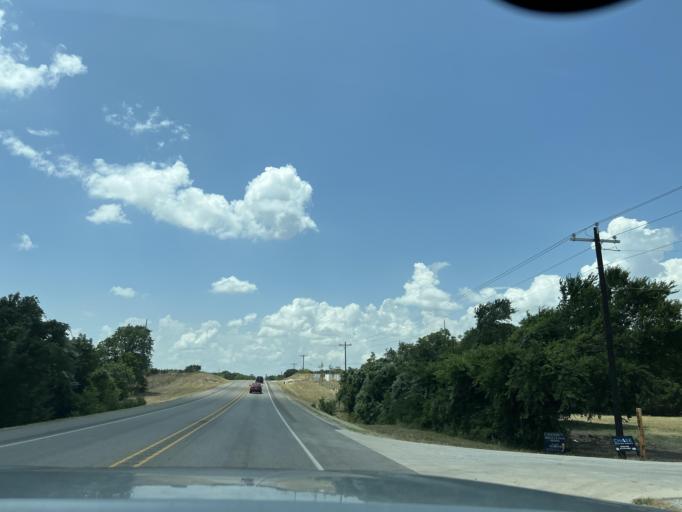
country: US
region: Texas
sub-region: Parker County
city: Weatherford
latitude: 32.8443
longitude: -97.7552
